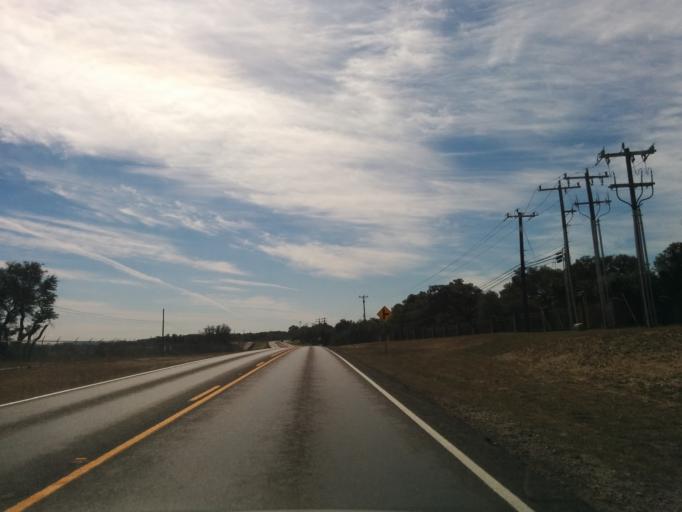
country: US
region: Texas
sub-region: Bexar County
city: Fair Oaks Ranch
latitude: 29.7230
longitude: -98.6236
